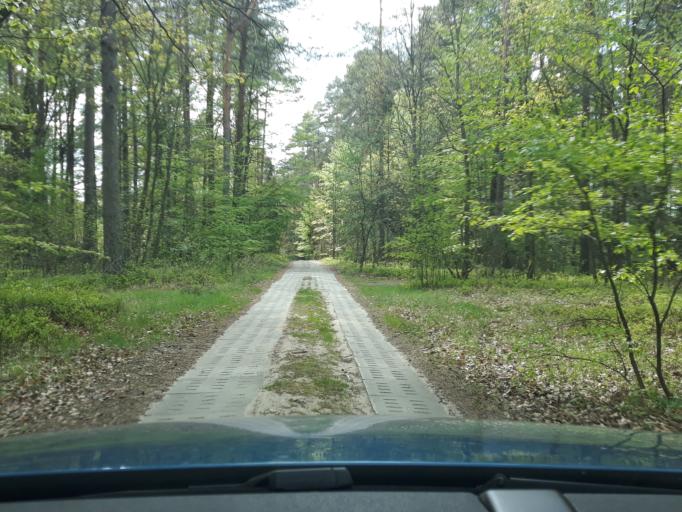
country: PL
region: Pomeranian Voivodeship
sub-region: Powiat czluchowski
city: Czluchow
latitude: 53.7193
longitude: 17.3409
